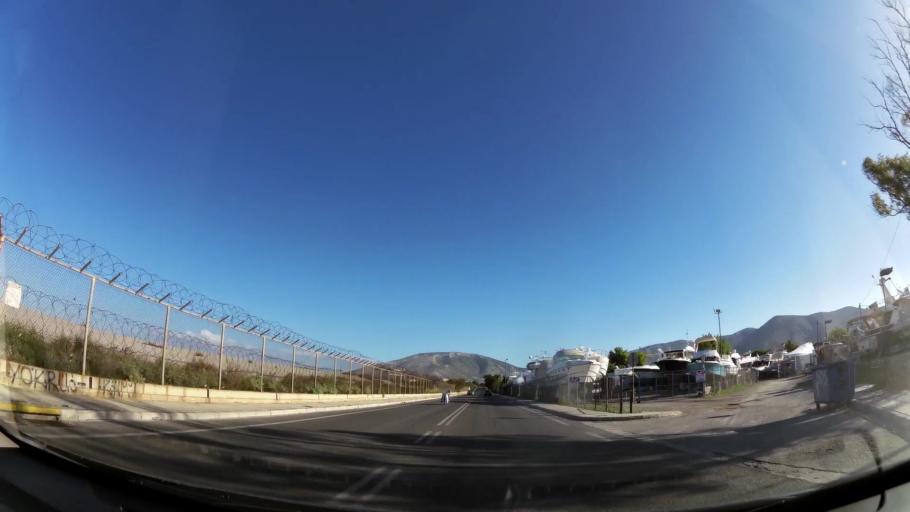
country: GR
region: Attica
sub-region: Nomarchia Athinas
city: Elliniko
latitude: 37.8732
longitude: 23.7404
